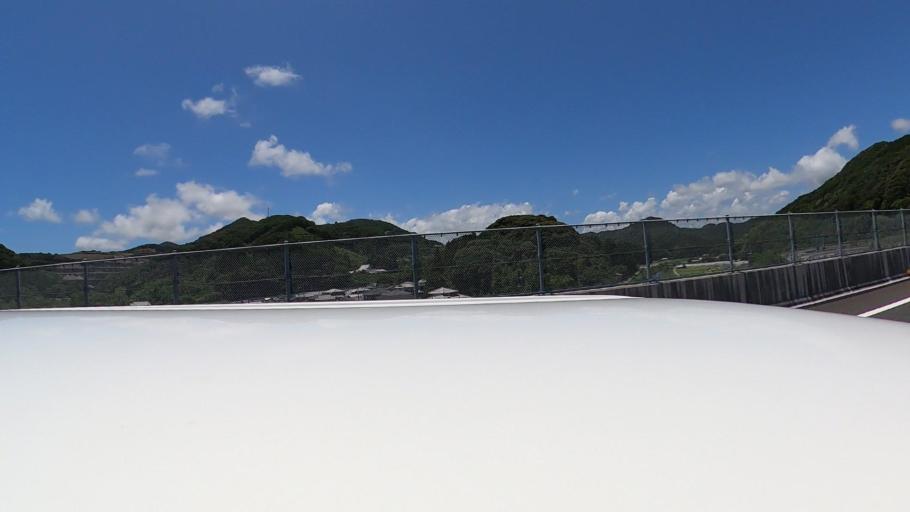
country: JP
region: Miyazaki
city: Nobeoka
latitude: 32.3992
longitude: 131.6176
